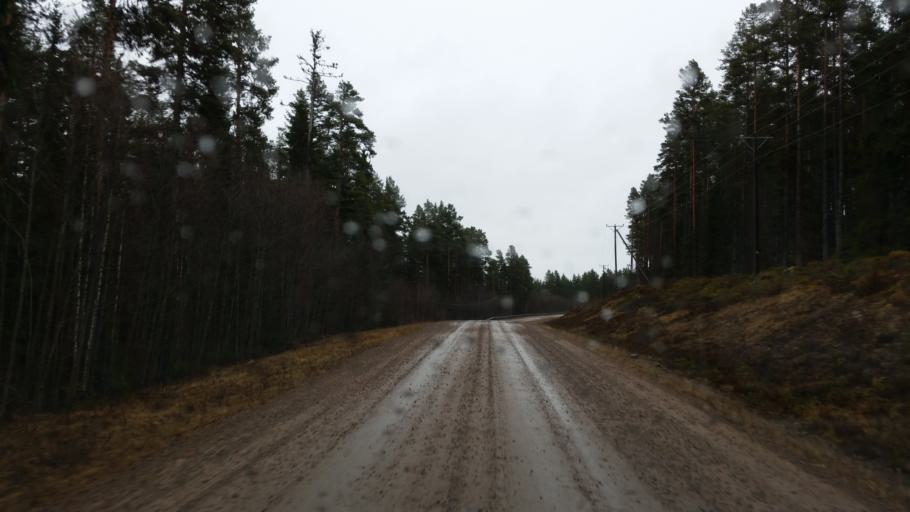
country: SE
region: Vaesternorrland
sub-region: Ange Kommun
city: Ange
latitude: 62.1670
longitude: 15.6540
